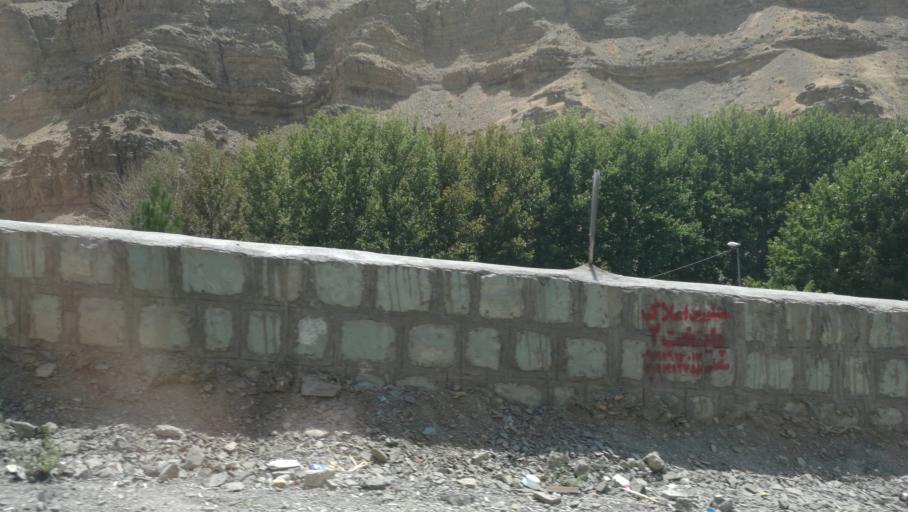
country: IR
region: Alborz
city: Karaj
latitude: 35.9469
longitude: 51.0710
